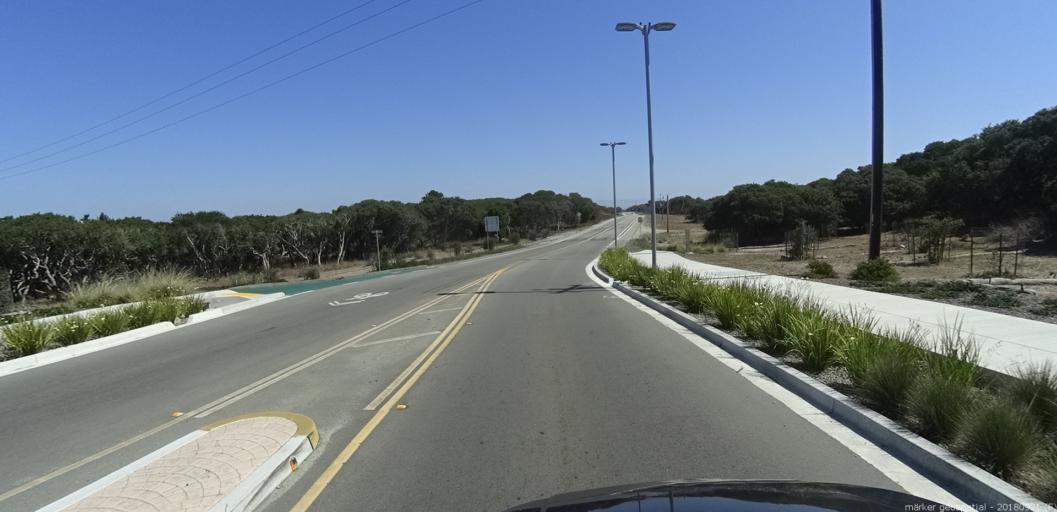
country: US
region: California
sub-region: Monterey County
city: Marina
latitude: 36.6546
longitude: -121.7855
